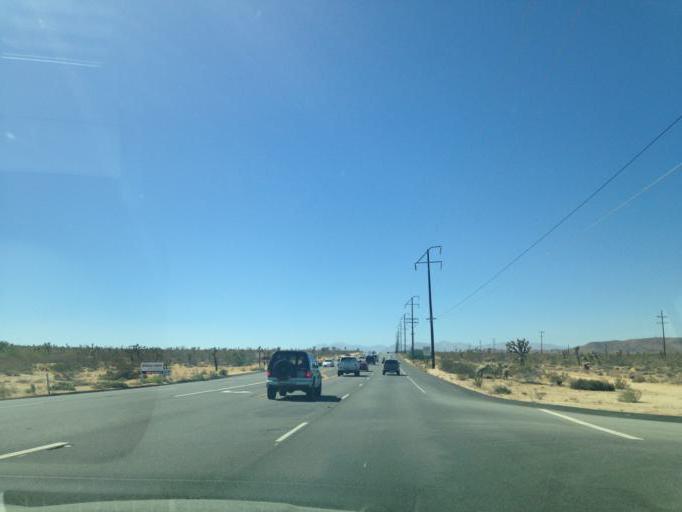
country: US
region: California
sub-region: San Bernardino County
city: Joshua Tree
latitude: 34.1351
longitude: -116.3342
